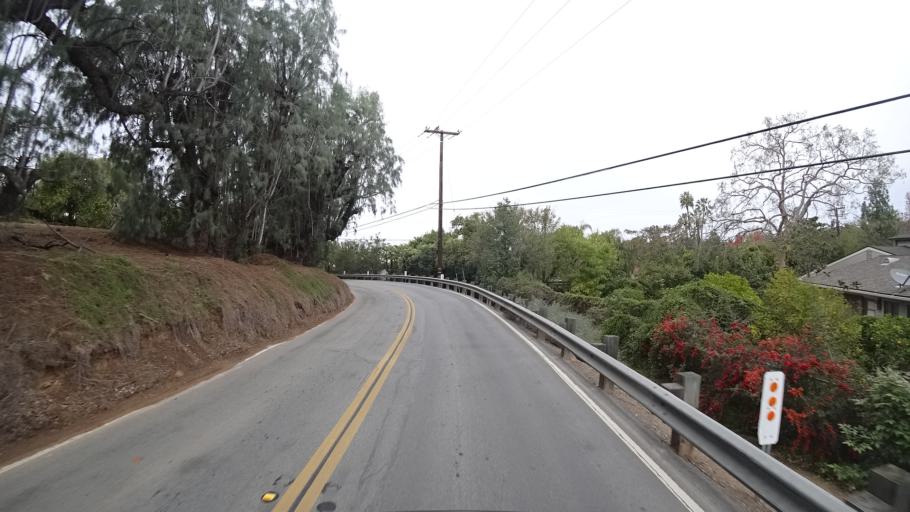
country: US
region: California
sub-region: Orange County
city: North Tustin
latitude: 33.7518
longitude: -117.7893
